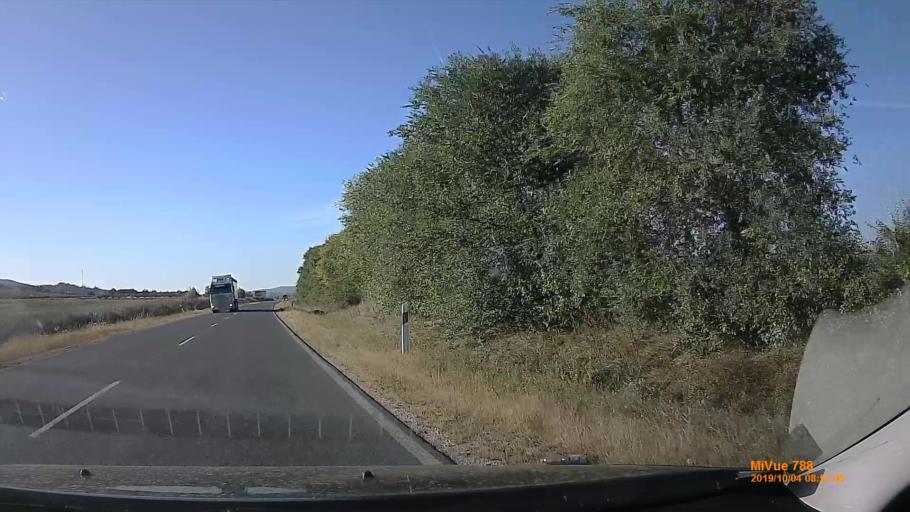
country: HU
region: Somogy
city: Balatonlelle
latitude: 46.7818
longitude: 17.7589
